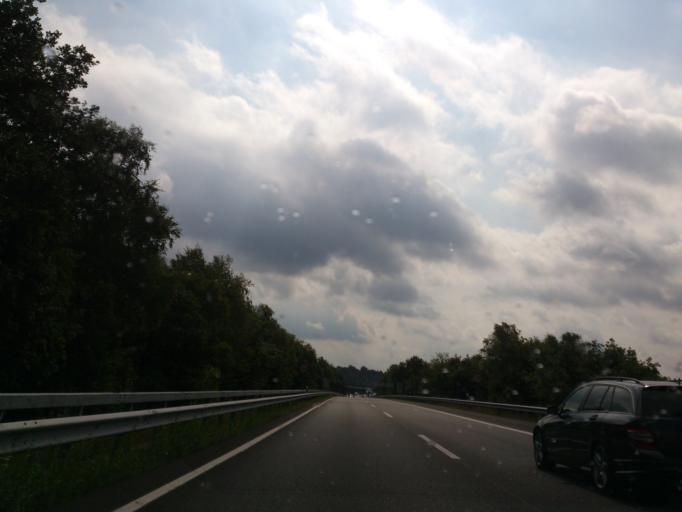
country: DE
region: Lower Saxony
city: Harmstorf
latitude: 53.3735
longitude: 10.0190
